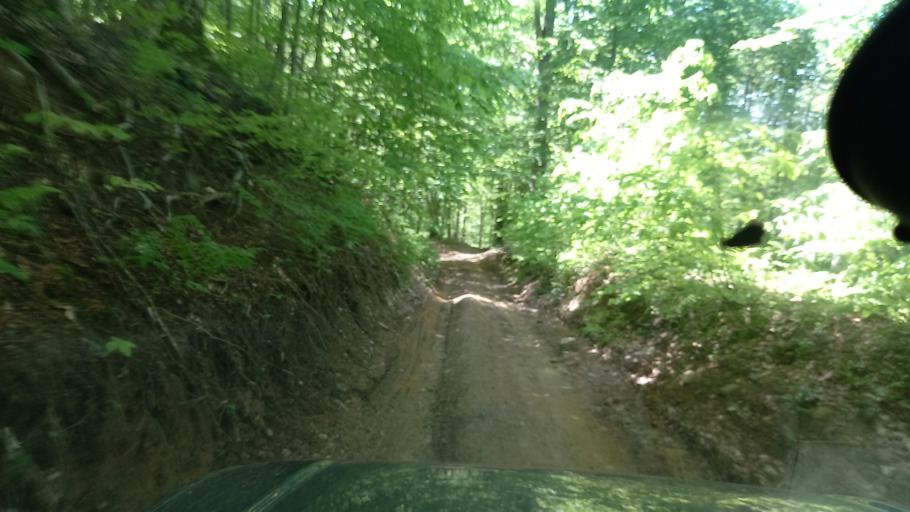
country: RU
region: Krasnodarskiy
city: Tuapse
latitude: 44.2512
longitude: 39.2903
